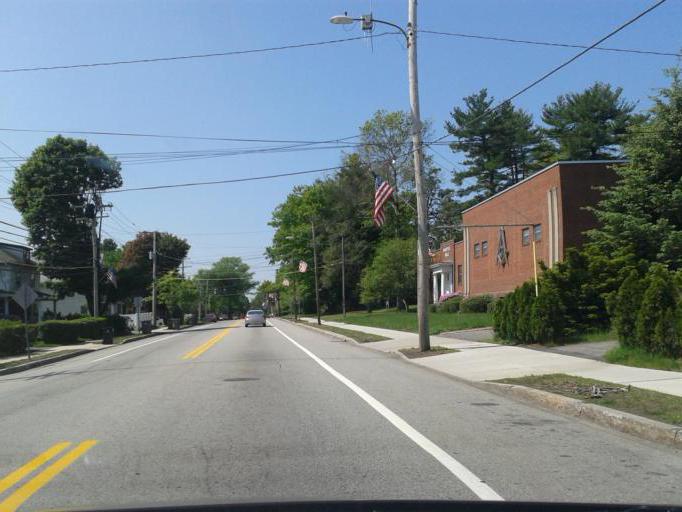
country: US
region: Massachusetts
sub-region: Middlesex County
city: Framingham
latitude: 42.2867
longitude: -71.4106
